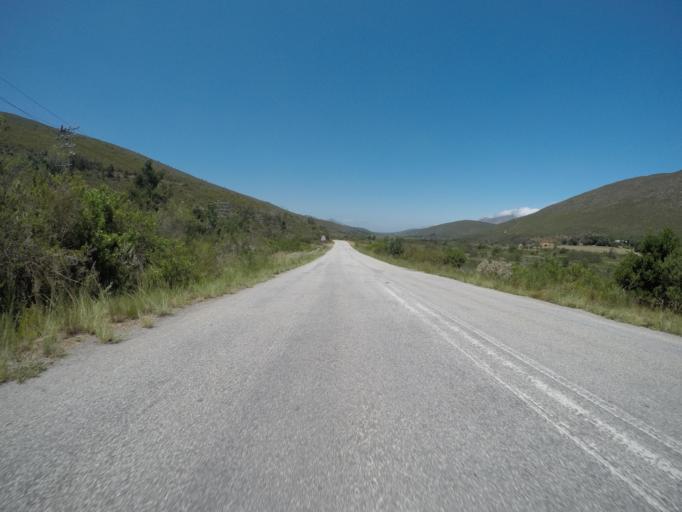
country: ZA
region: Eastern Cape
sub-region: Cacadu District Municipality
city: Kareedouw
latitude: -33.8665
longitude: 24.0165
